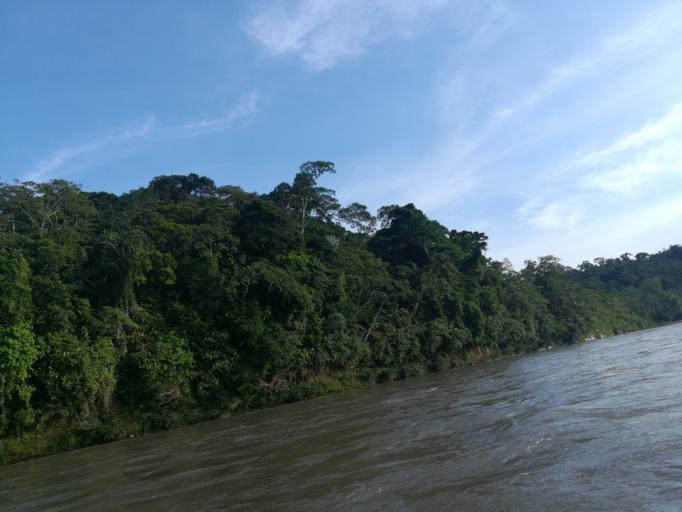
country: EC
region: Orellana
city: Boca Suno
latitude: -0.8664
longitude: -77.2502
